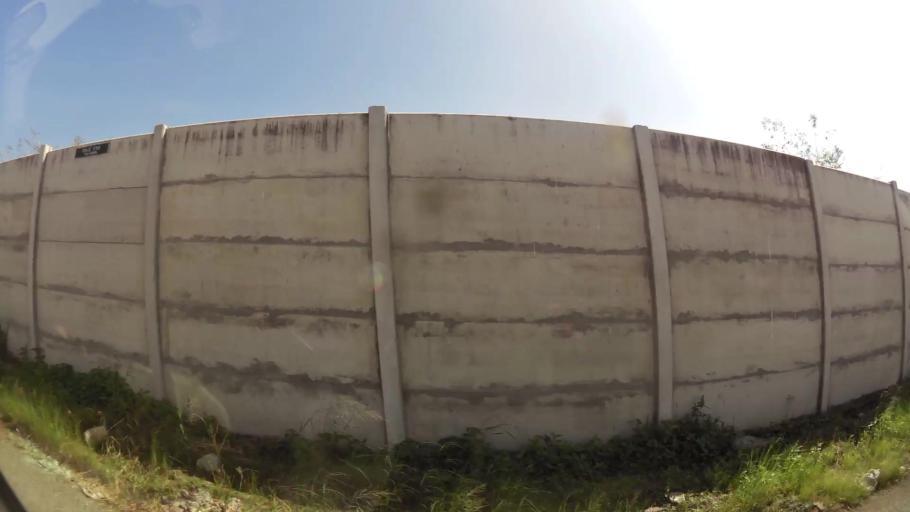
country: EC
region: Guayas
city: Guayaquil
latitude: -2.1880
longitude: -79.9133
